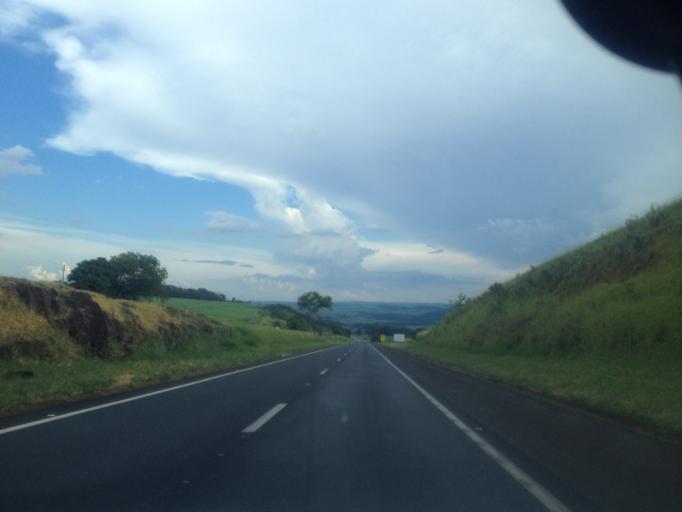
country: BR
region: Sao Paulo
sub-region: Santa Rita Do Passa Quatro
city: Santa Rita do Passa Quatro
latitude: -21.7011
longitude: -47.5961
